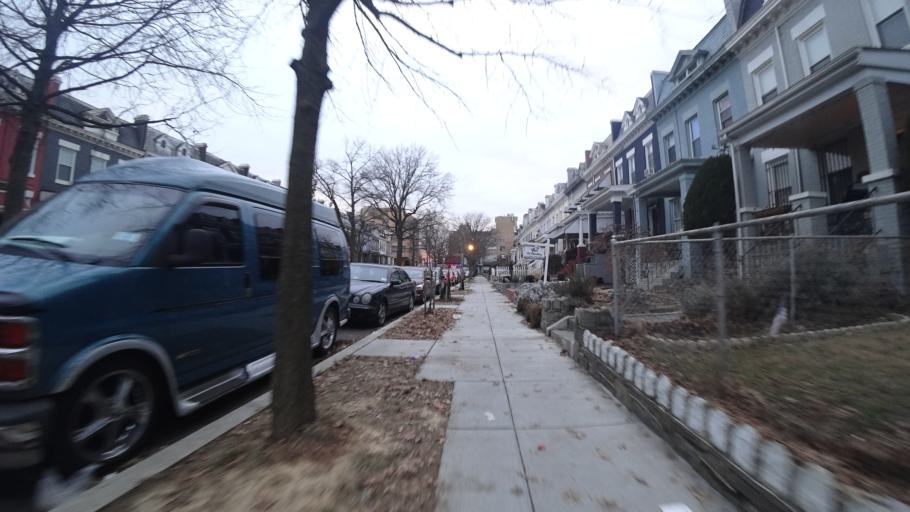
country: US
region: Washington, D.C.
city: Washington, D.C.
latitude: 38.9314
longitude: -77.0221
